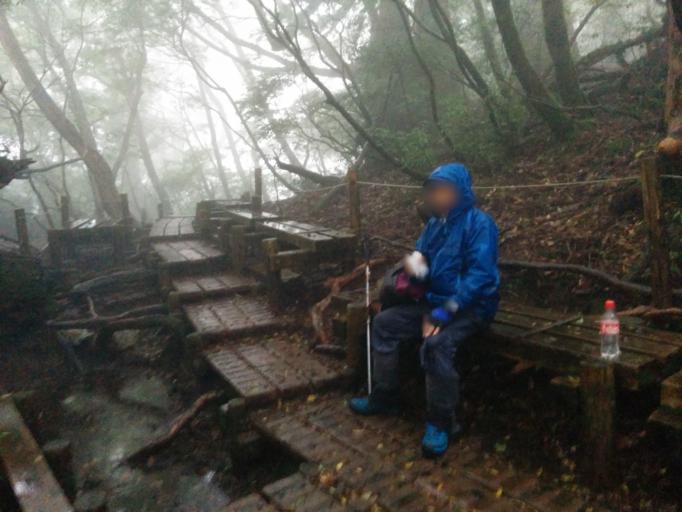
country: JP
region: Kagoshima
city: Nishinoomote
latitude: 30.3612
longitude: 130.5327
